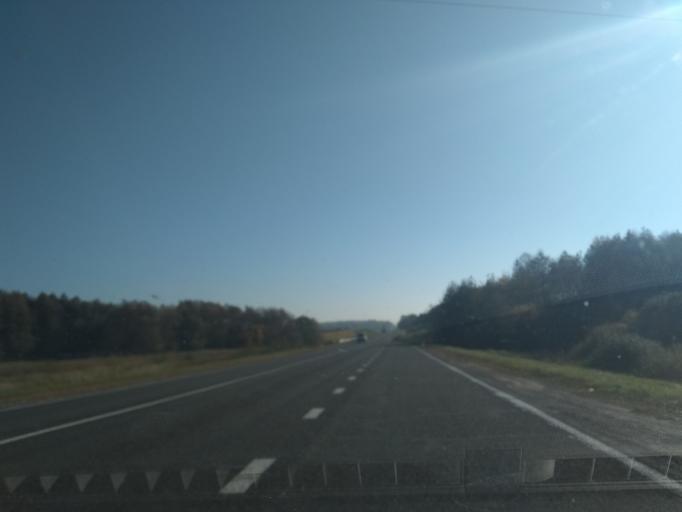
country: BY
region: Grodnenskaya
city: Slonim
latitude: 53.1157
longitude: 25.1433
